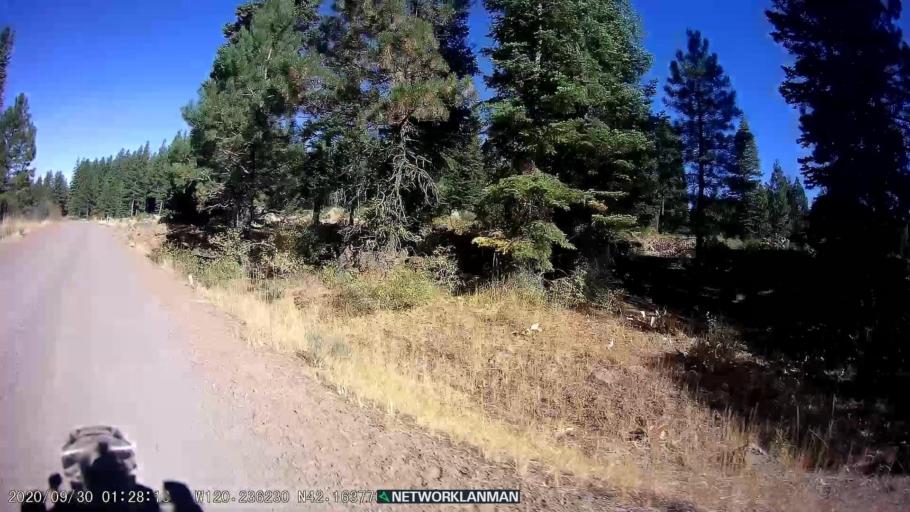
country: US
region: Oregon
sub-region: Lake County
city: Lakeview
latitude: 42.1667
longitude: -120.2410
